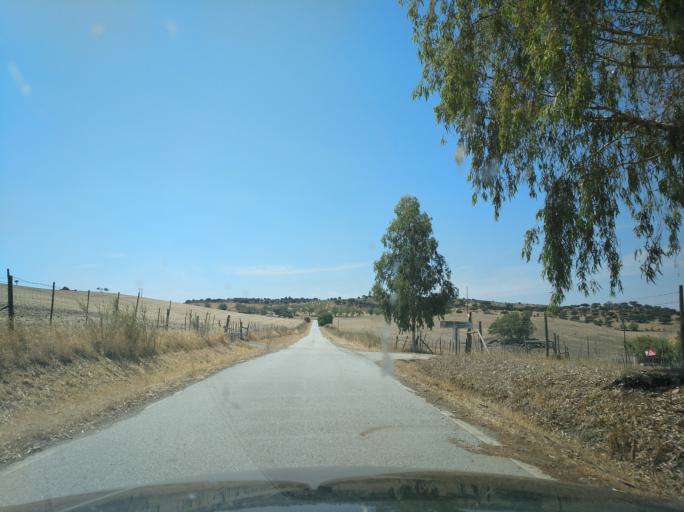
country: PT
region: Portalegre
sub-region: Campo Maior
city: Campo Maior
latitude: 38.9622
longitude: -7.1155
